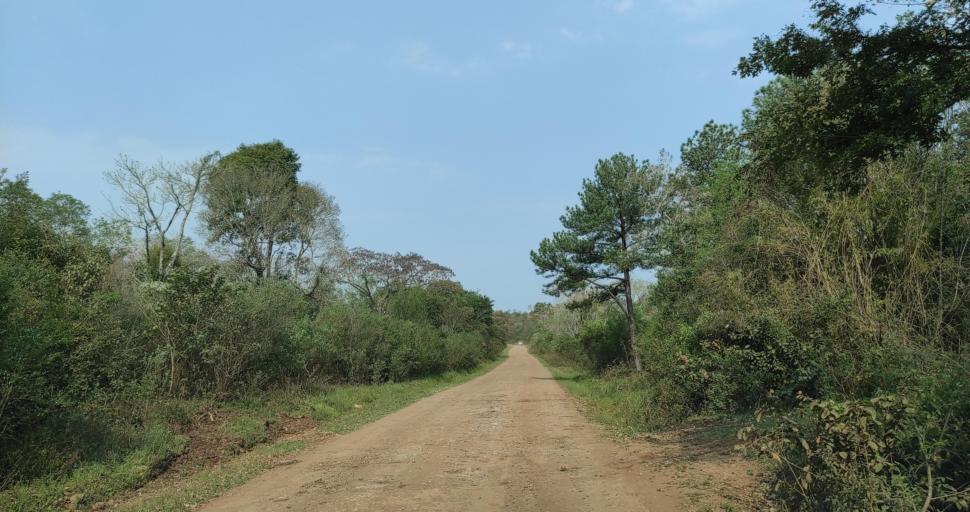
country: AR
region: Misiones
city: Cerro Cora
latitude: -27.5278
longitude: -55.5955
